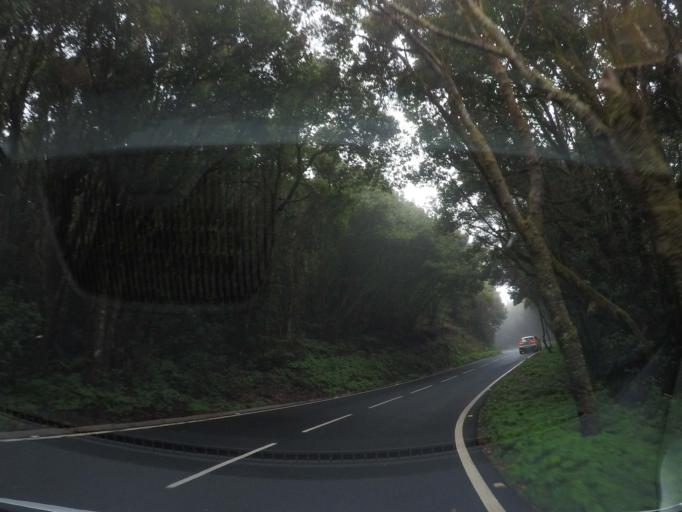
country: ES
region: Canary Islands
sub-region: Provincia de Santa Cruz de Tenerife
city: Vallehermosa
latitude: 28.1428
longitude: -17.2850
